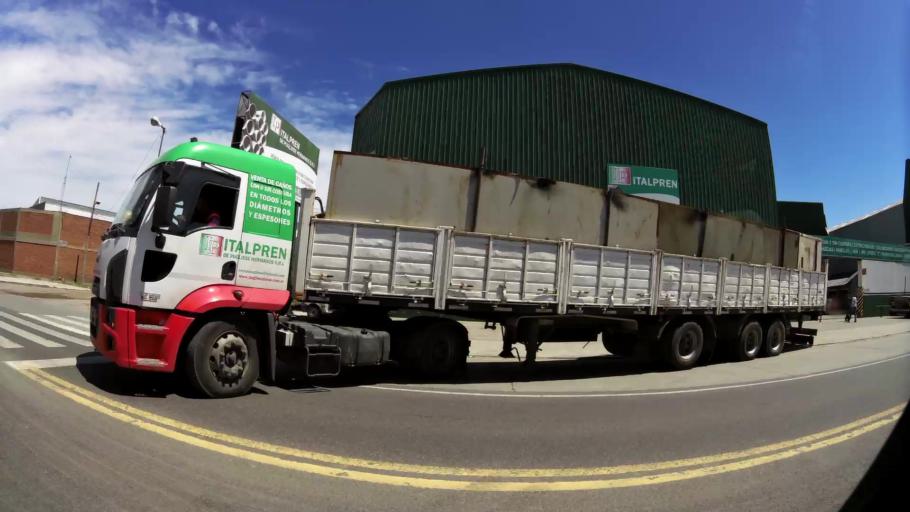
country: AR
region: Buenos Aires
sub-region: Partido de Quilmes
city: Quilmes
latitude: -34.7430
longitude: -58.3150
